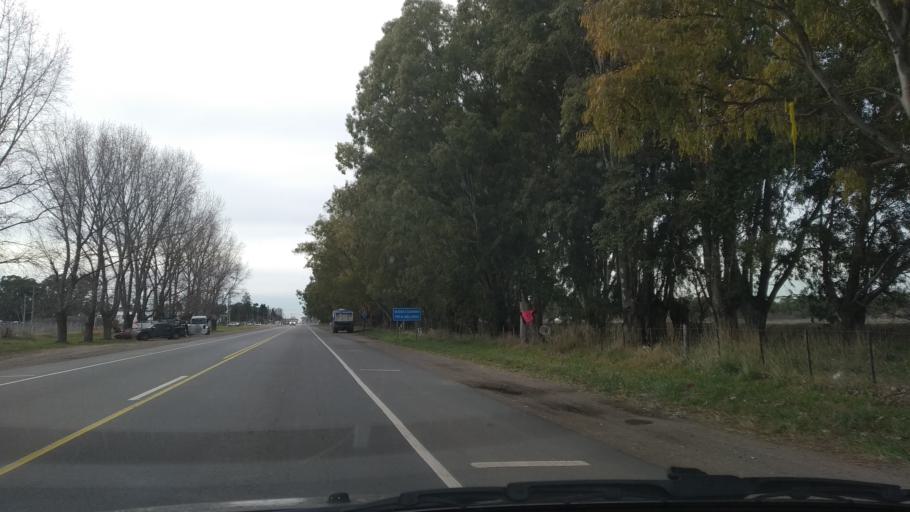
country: AR
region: Buenos Aires
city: Olavarria
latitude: -36.9662
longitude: -60.2672
